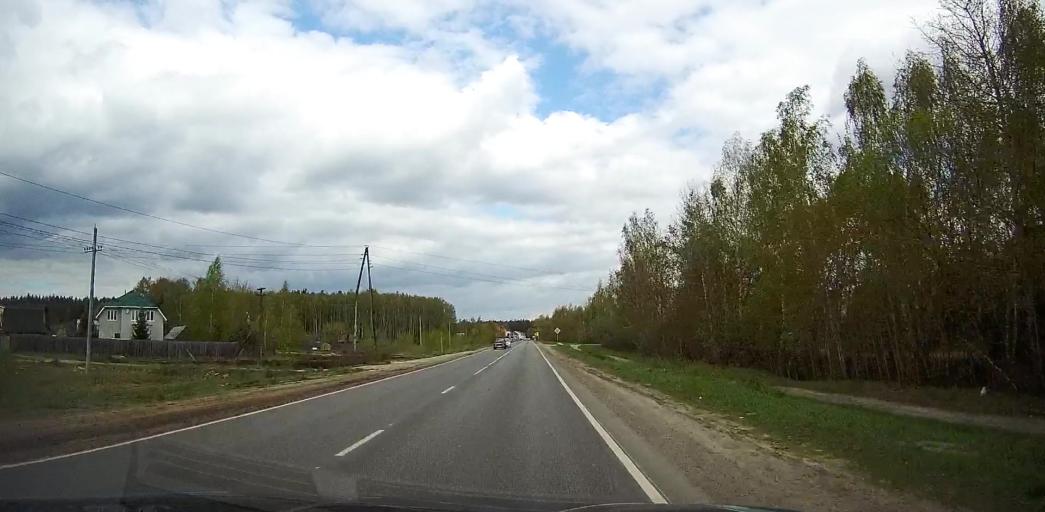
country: RU
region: Moskovskaya
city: Ashitkovo
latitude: 55.4322
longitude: 38.5783
